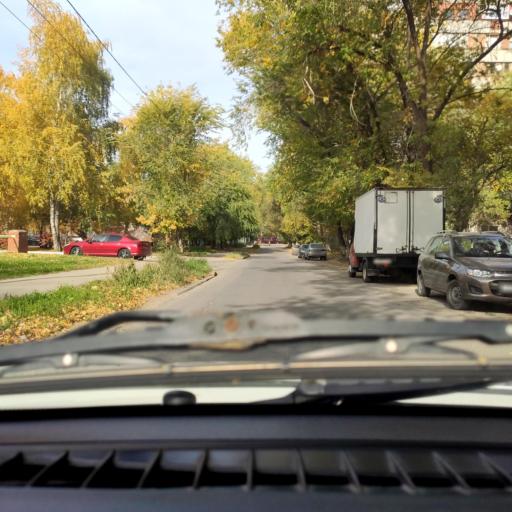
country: RU
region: Samara
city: Tol'yatti
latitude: 53.5048
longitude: 49.4229
